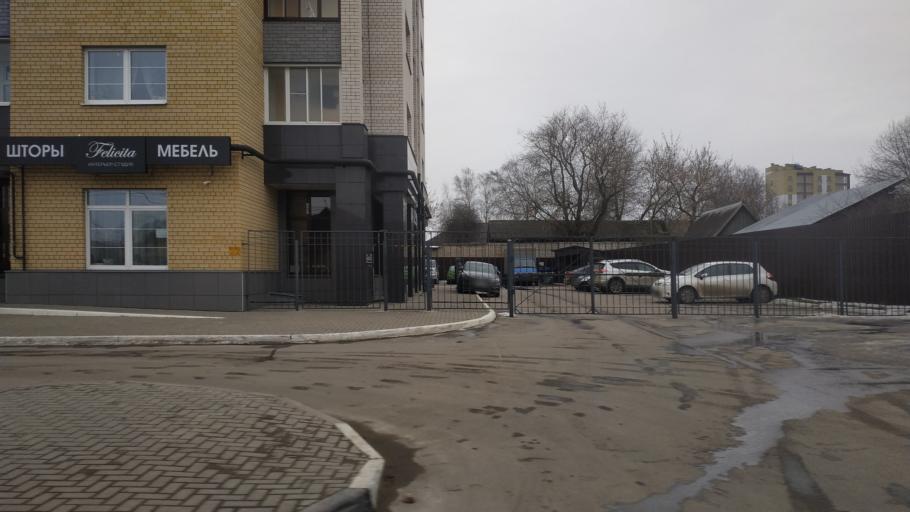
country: RU
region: Tverskaya
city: Tver
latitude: 56.8787
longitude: 35.8930
